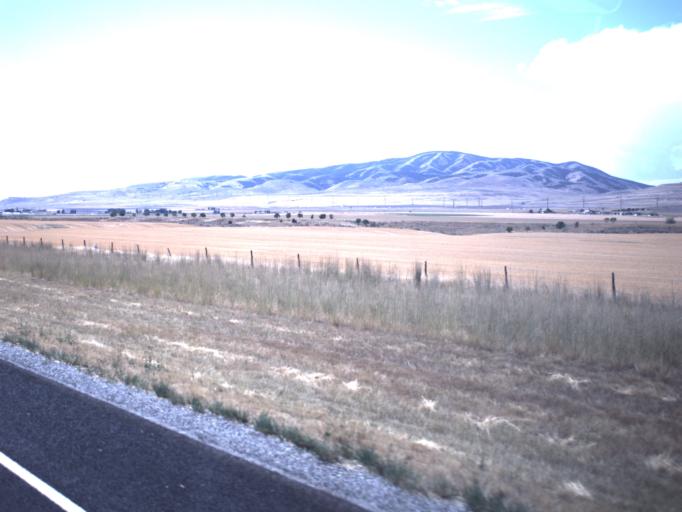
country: US
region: Utah
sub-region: Box Elder County
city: Garland
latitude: 41.8574
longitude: -112.1466
